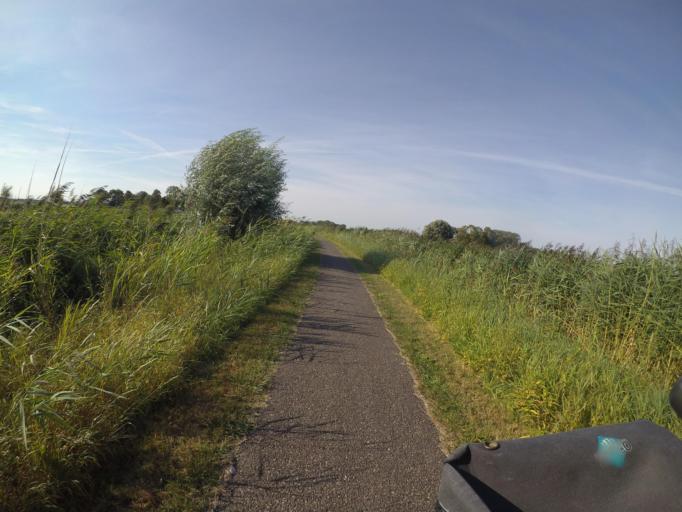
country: NL
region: Friesland
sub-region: Gemeente Dantumadiel
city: Rinsumageast
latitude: 53.3198
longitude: 5.9509
